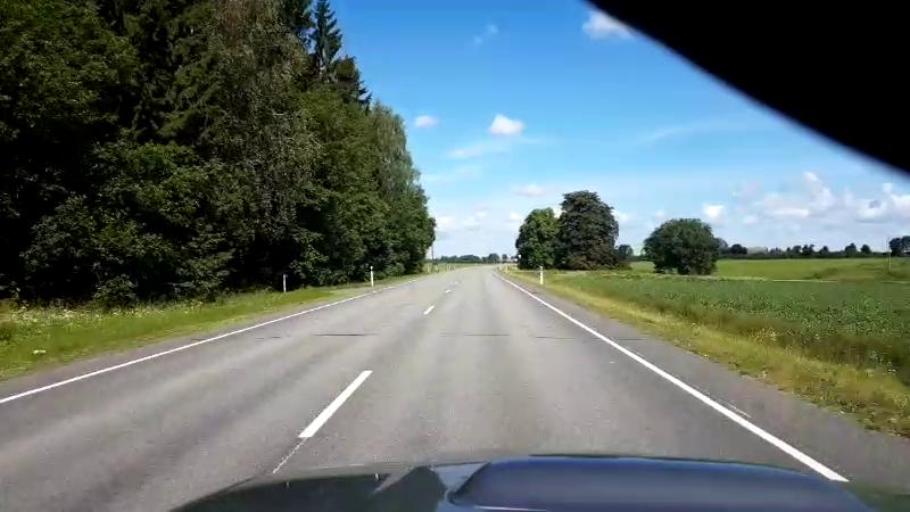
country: EE
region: Jaervamaa
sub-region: Jaerva-Jaani vald
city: Jarva-Jaani
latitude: 59.1645
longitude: 25.7600
